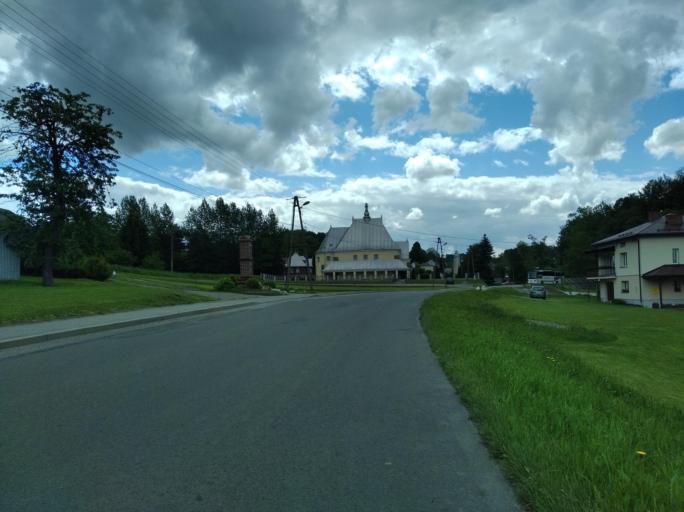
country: PL
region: Subcarpathian Voivodeship
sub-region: Powiat brzozowski
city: Zmiennica
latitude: 49.6943
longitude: 21.9351
